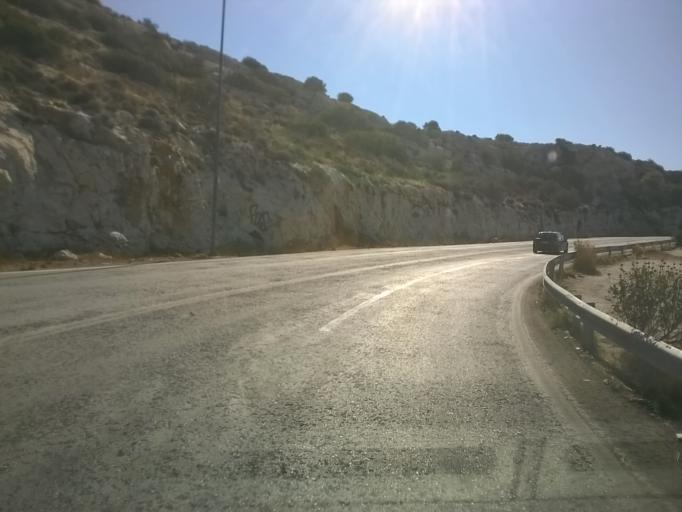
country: GR
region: Attica
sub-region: Nomarchia Anatolikis Attikis
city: Vouliagmeni
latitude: 37.8028
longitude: 23.7869
